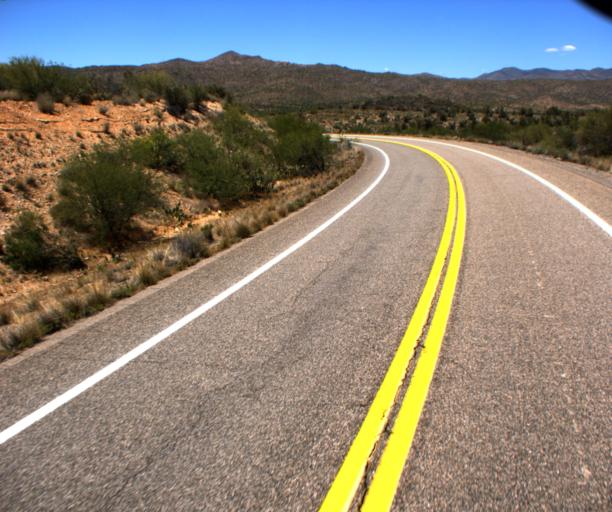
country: US
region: Arizona
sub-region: Yavapai County
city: Bagdad
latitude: 34.5157
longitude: -113.0754
